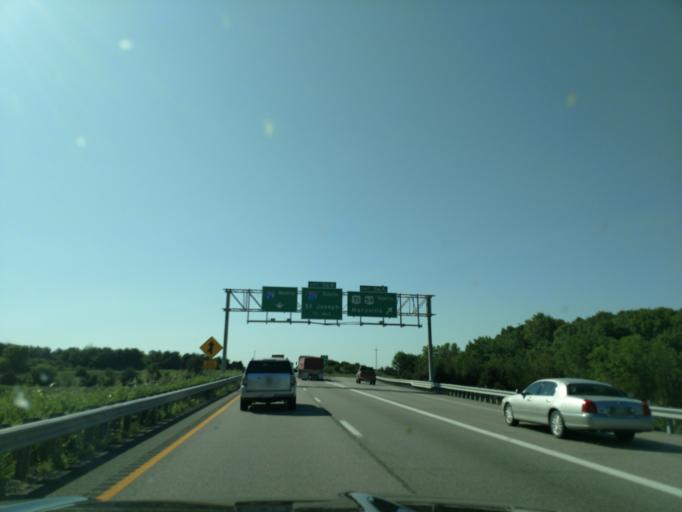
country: US
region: Missouri
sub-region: Andrew County
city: Savannah
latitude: 39.8850
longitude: -94.8541
